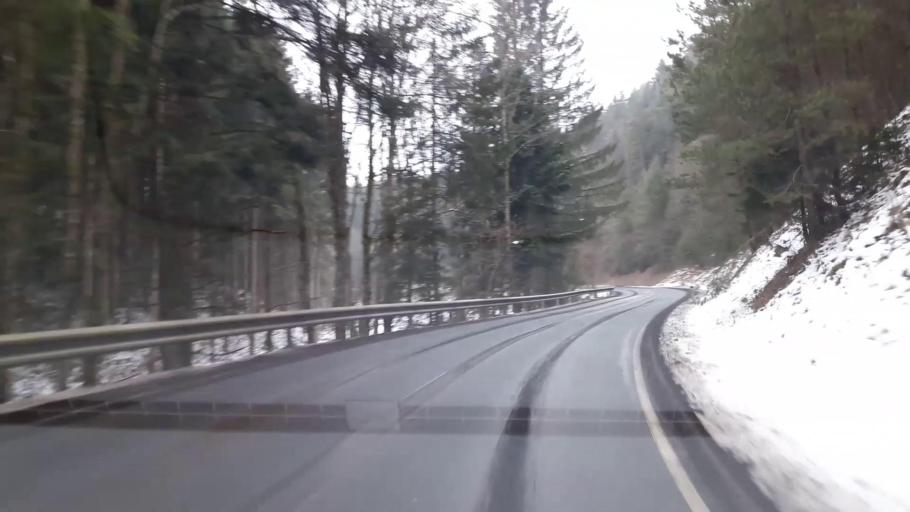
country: AT
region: Lower Austria
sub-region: Politischer Bezirk Neunkirchen
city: Feistritz am Wechsel
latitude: 47.5546
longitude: 16.0739
